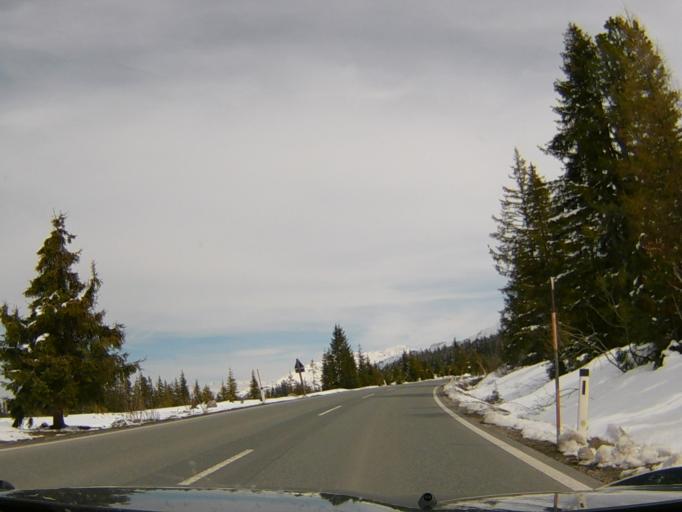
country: AT
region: Salzburg
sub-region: Politischer Bezirk Zell am See
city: Krimml
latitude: 47.2417
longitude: 12.1417
